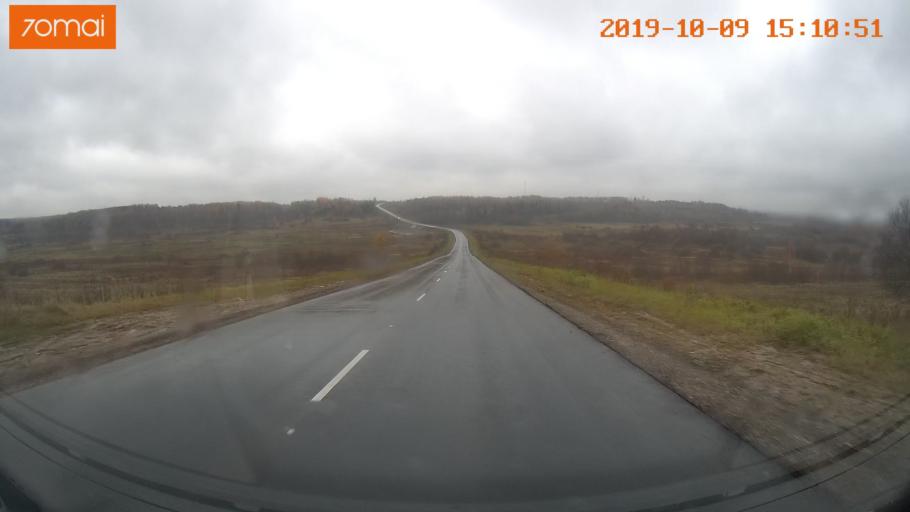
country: RU
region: Kostroma
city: Susanino
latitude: 58.1731
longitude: 41.6356
